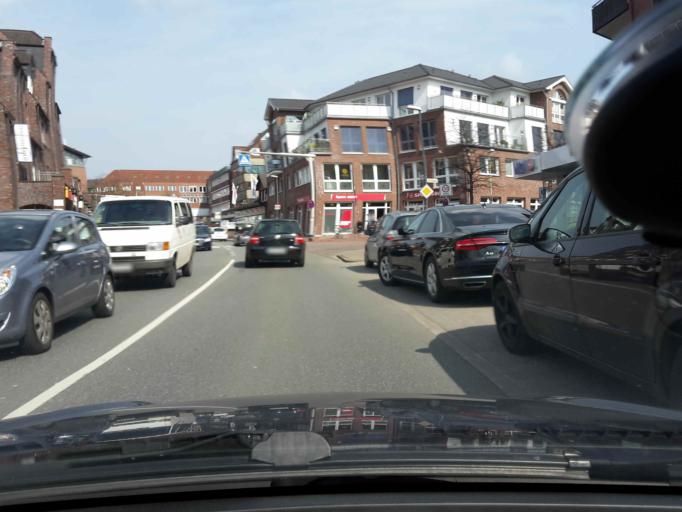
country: DE
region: Lower Saxony
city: Buchholz in der Nordheide
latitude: 53.3273
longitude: 9.8825
